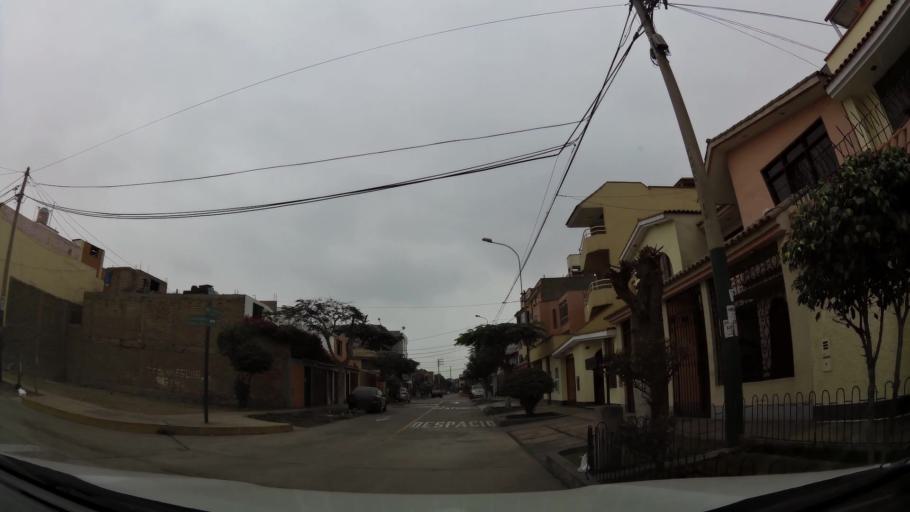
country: PE
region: Lima
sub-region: Lima
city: Surco
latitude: -12.1405
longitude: -76.9857
